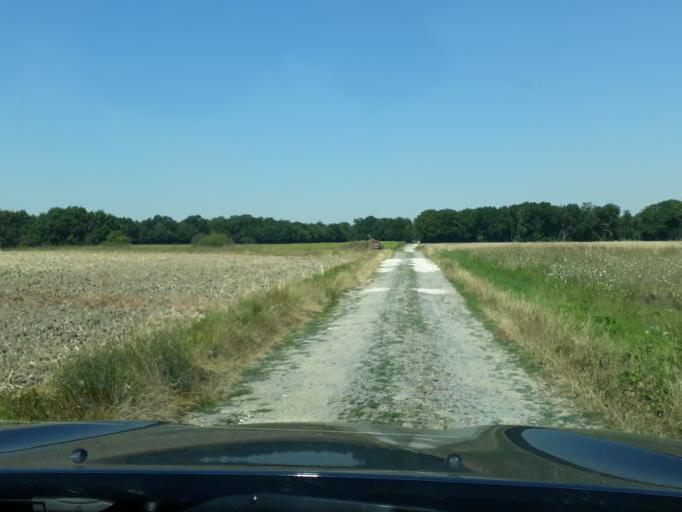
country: FR
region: Centre
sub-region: Departement du Loiret
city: Chevilly
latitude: 47.9935
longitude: 1.9113
